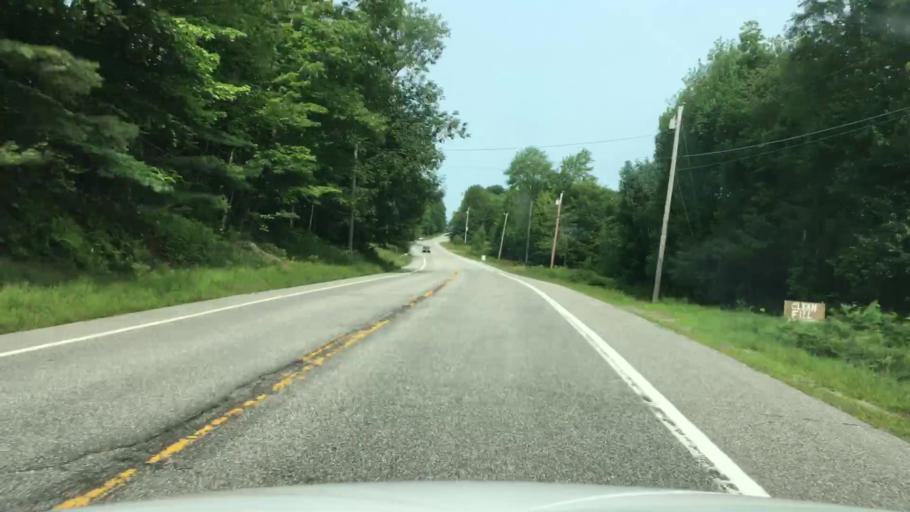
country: US
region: Maine
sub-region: Kennebec County
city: Wayne
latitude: 44.3694
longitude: -70.0921
